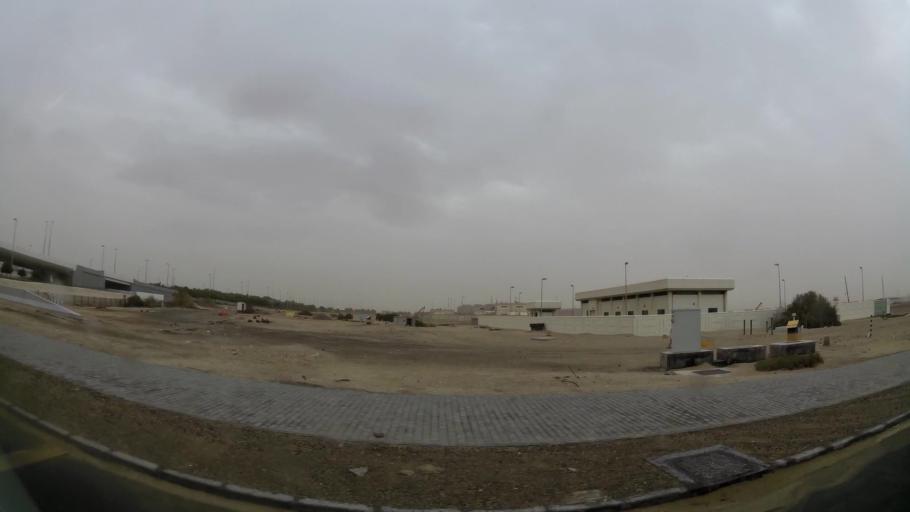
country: AE
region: Abu Dhabi
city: Abu Dhabi
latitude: 24.4462
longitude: 54.6172
